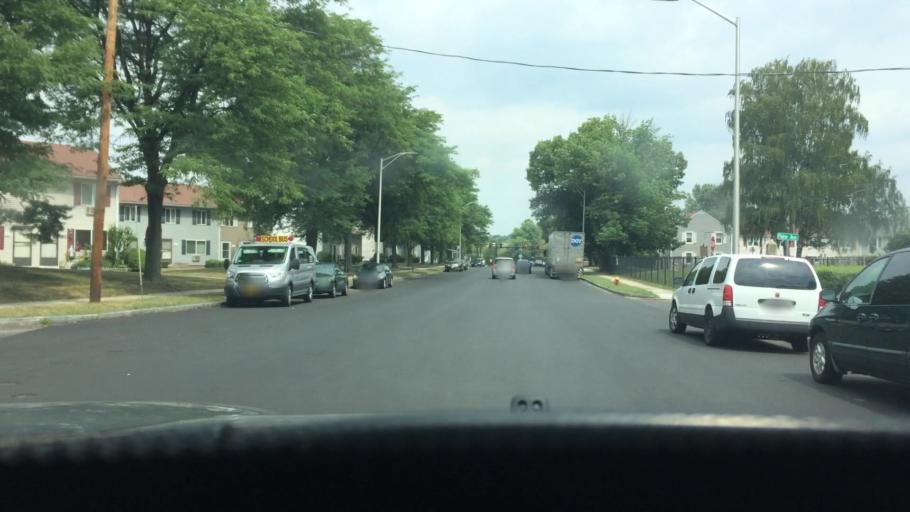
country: US
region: Massachusetts
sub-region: Hampden County
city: Chicopee
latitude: 42.1550
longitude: -72.5807
